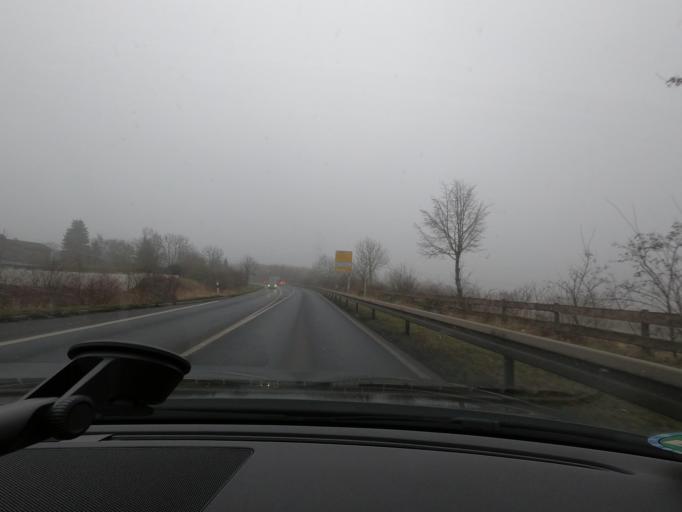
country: DE
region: North Rhine-Westphalia
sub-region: Regierungsbezirk Koln
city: Merzenich
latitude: 50.8396
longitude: 6.5203
